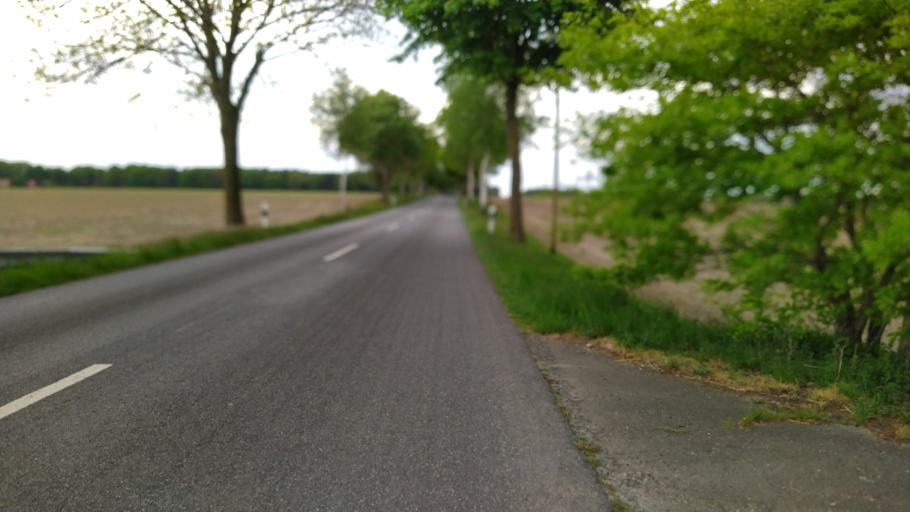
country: DE
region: Lower Saxony
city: Farven
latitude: 53.4295
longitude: 9.3119
